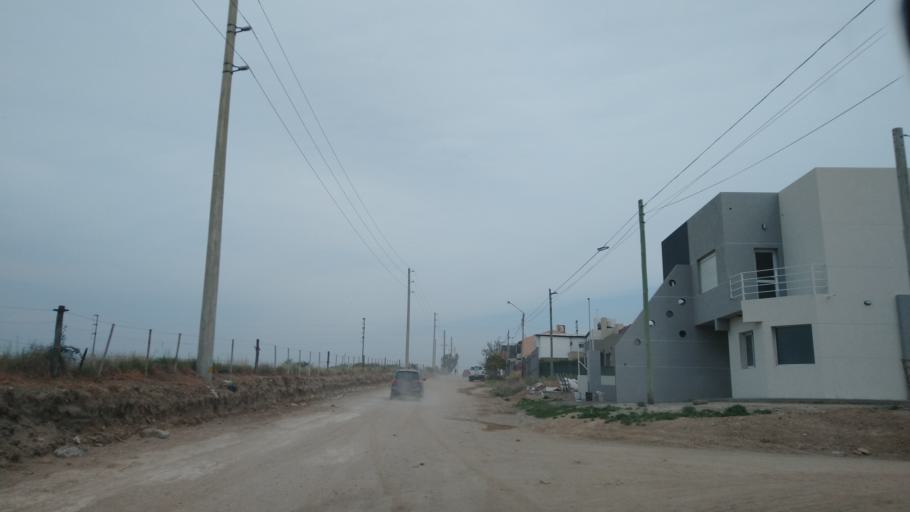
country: AR
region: Buenos Aires
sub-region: Partido de Bahia Blanca
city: Bahia Blanca
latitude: -38.6974
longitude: -62.2338
